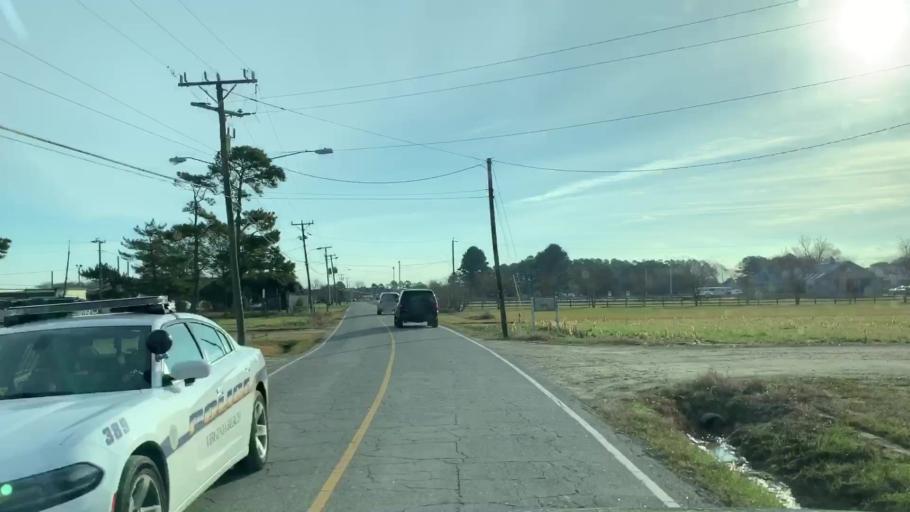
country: US
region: Virginia
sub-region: City of Virginia Beach
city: Virginia Beach
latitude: 36.6904
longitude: -76.0115
